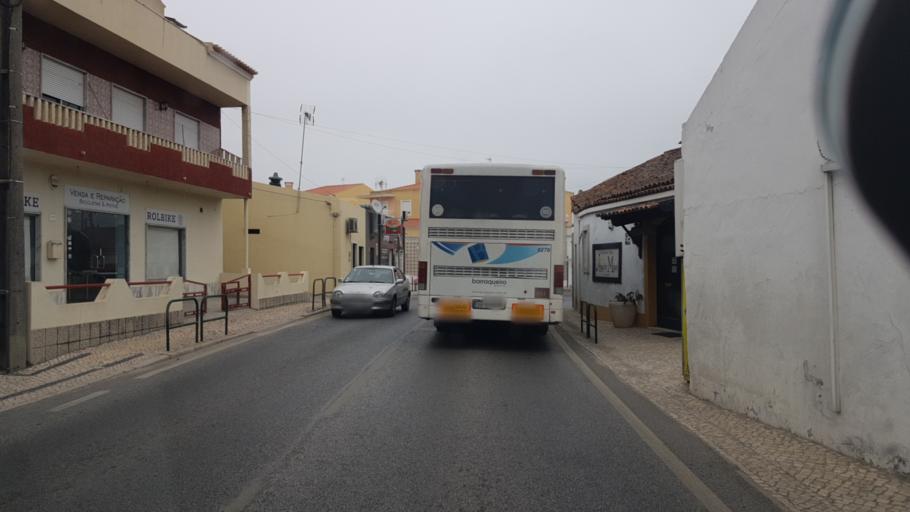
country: PT
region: Lisbon
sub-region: Torres Vedras
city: Silveira
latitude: 39.0907
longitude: -9.3188
